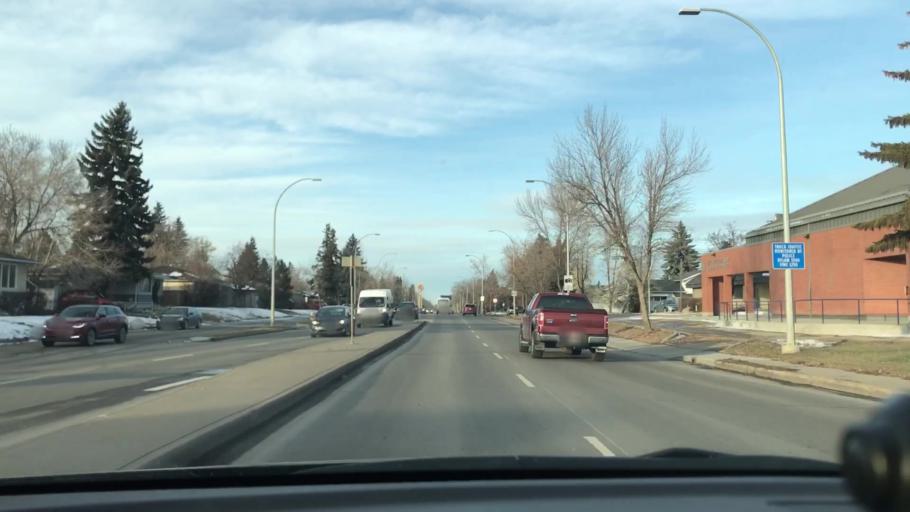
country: CA
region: Alberta
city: Edmonton
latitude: 53.5259
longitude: -113.4428
